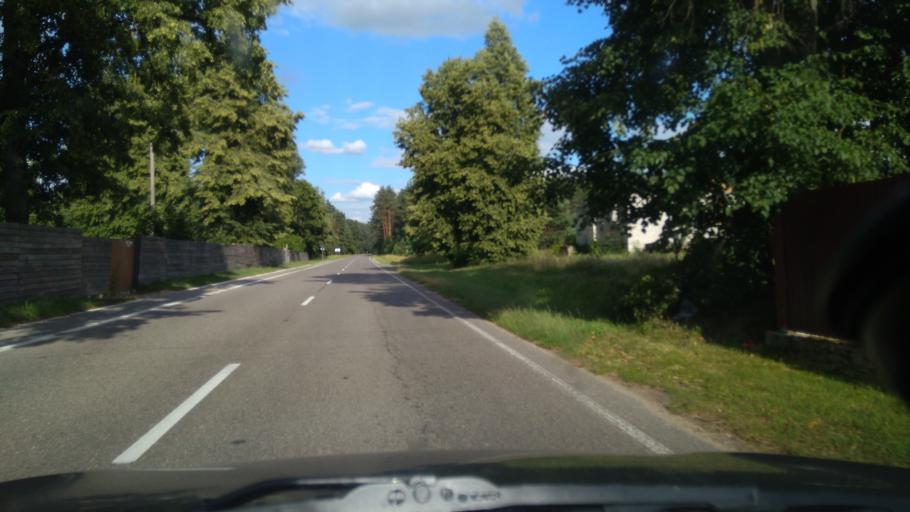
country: BY
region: Grodnenskaya
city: Masty
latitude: 53.3490
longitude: 24.6443
